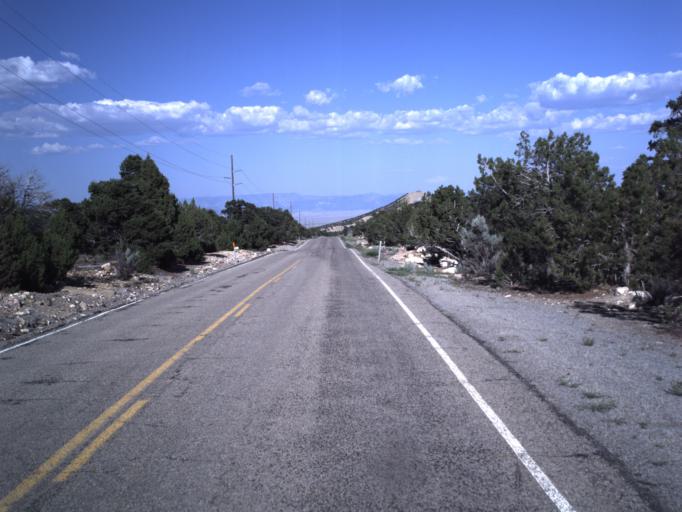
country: US
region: Utah
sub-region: Emery County
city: Huntington
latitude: 39.4841
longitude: -110.9762
